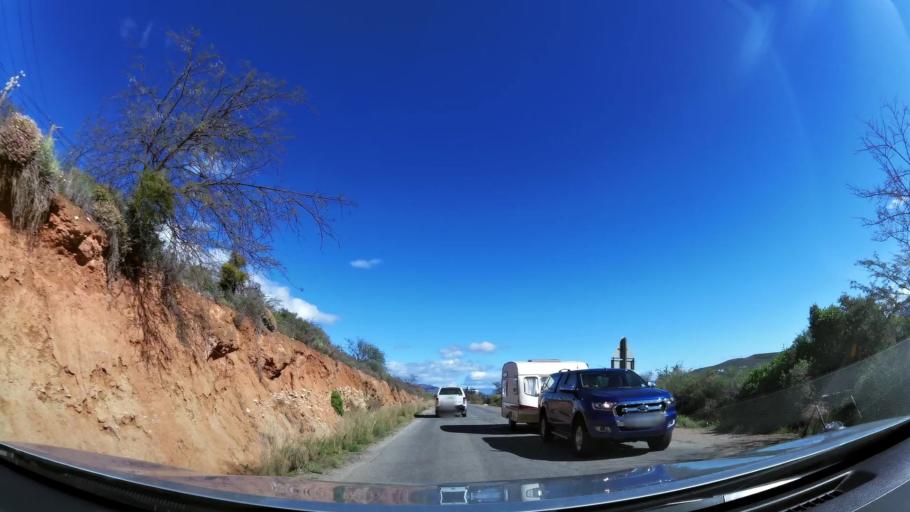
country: ZA
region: Western Cape
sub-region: Cape Winelands District Municipality
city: Ashton
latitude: -33.8285
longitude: 20.0863
